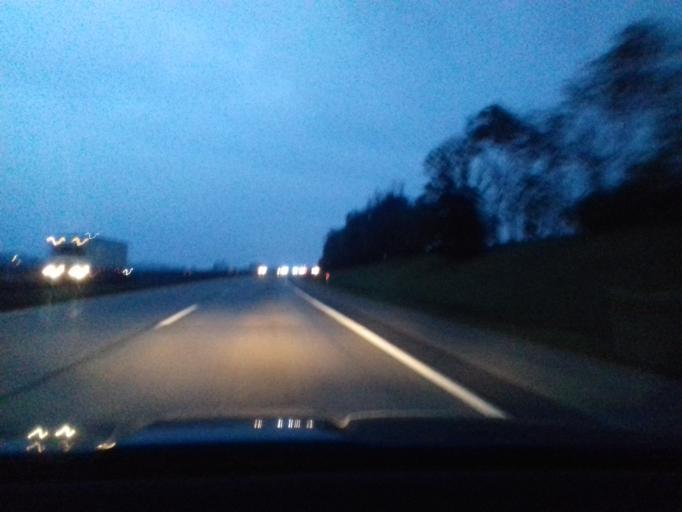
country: CZ
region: Vysocina
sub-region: Okres Zd'ar nad Sazavou
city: Velke Mezirici
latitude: 49.3298
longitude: 16.0735
